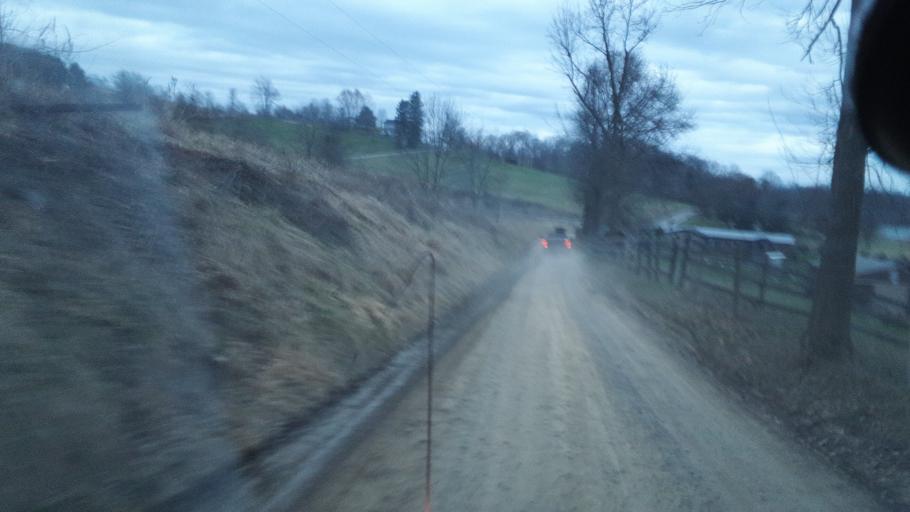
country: US
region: Ohio
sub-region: Coshocton County
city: West Lafayette
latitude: 40.3537
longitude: -81.7676
